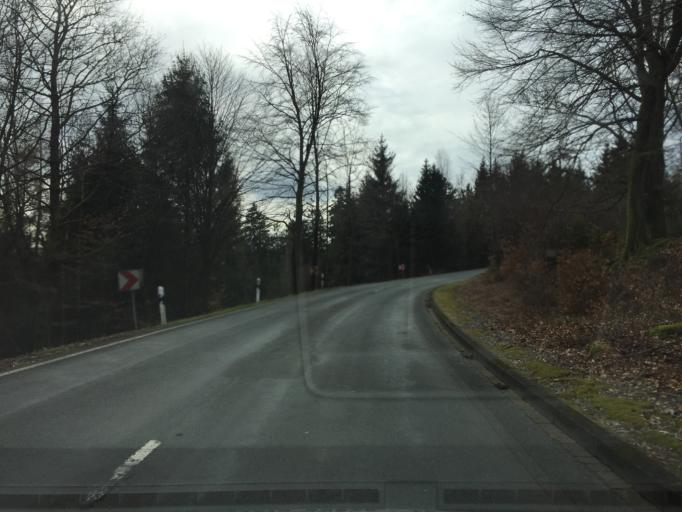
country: DE
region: North Rhine-Westphalia
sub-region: Regierungsbezirk Detmold
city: Detmold
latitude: 51.9138
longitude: 8.8497
